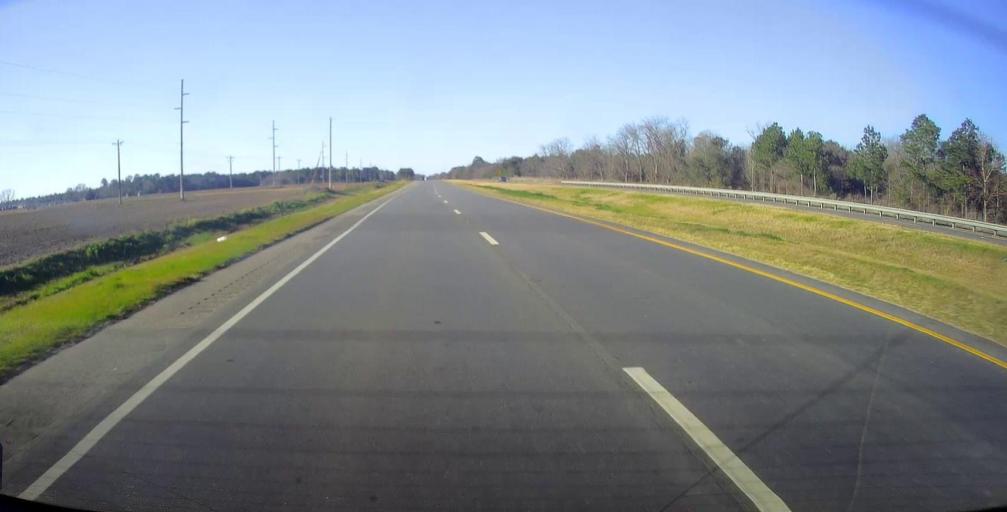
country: US
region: Georgia
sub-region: Lee County
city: Leesburg
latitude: 31.7942
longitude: -84.2017
